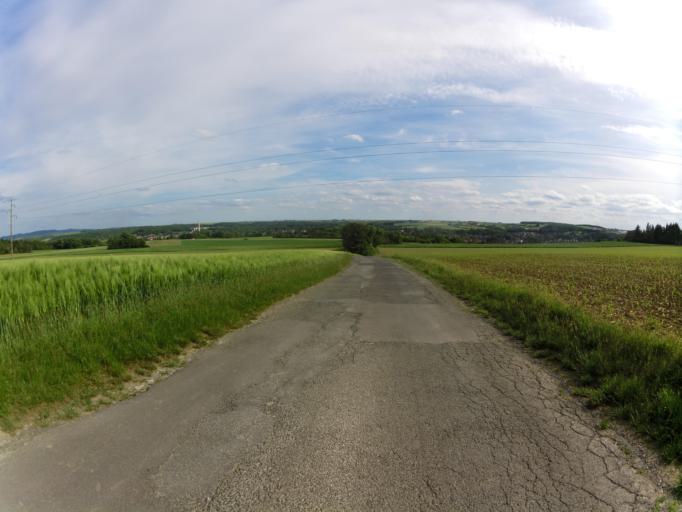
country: DE
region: Bavaria
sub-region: Regierungsbezirk Unterfranken
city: Ochsenfurt
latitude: 49.6778
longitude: 10.0669
